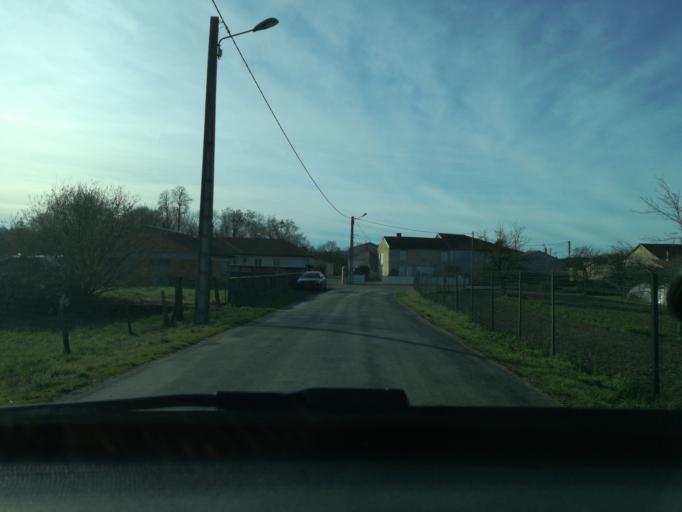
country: FR
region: Lorraine
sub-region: Departement de la Meuse
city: Revigny-sur-Ornain
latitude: 48.8218
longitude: 5.0495
